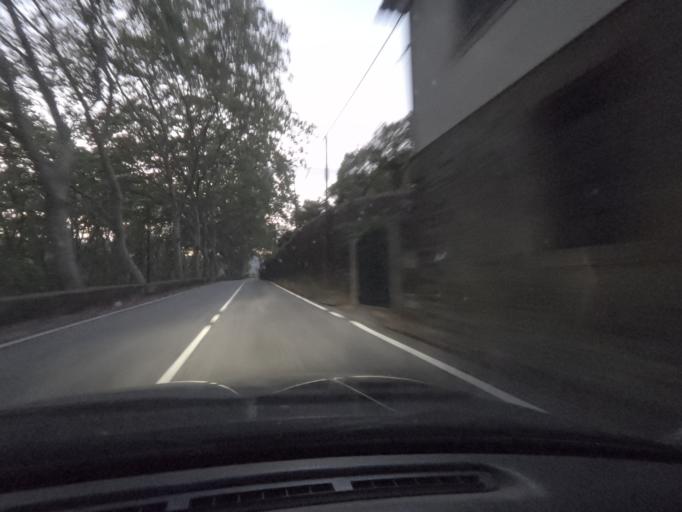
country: PT
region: Vila Real
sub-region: Peso da Regua
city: Godim
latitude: 41.1550
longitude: -7.8360
